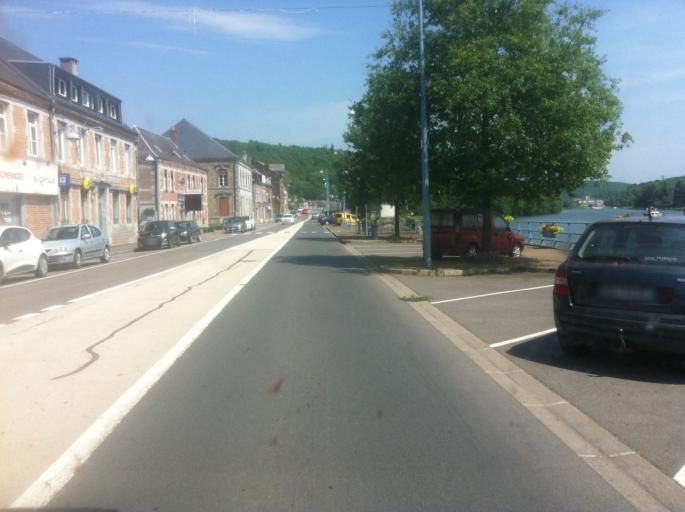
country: FR
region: Champagne-Ardenne
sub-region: Departement des Ardennes
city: Vireux-Wallerand
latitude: 50.0855
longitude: 4.7247
